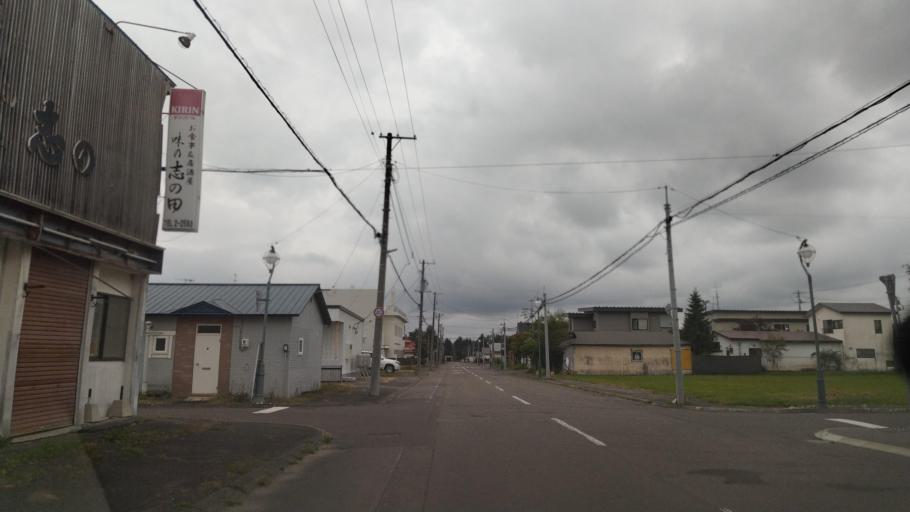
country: JP
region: Hokkaido
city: Otofuke
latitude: 43.2313
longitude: 143.2931
